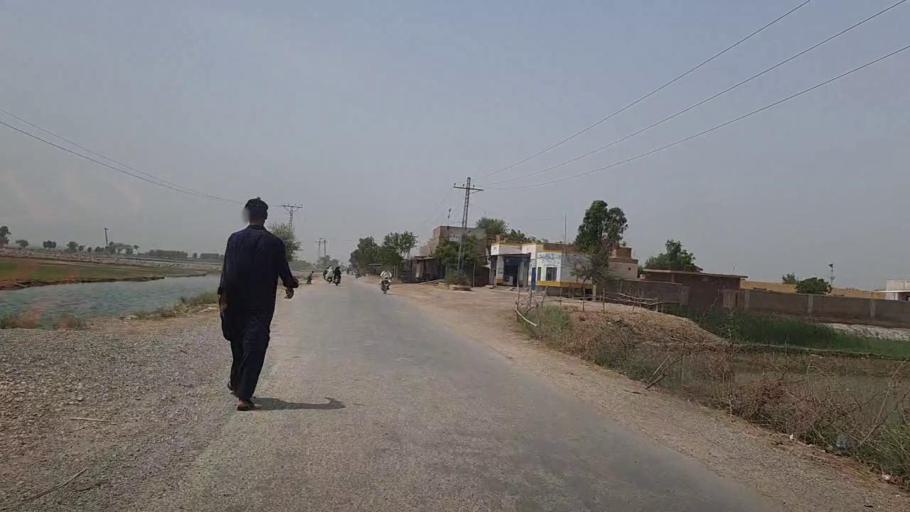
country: PK
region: Sindh
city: Radhan
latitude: 27.1686
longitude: 67.9458
